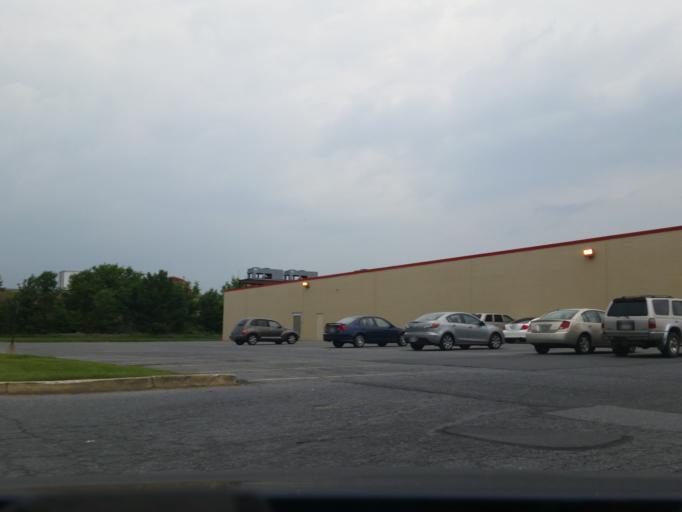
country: US
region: Pennsylvania
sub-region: Lebanon County
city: Fredericksburg
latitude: 40.4501
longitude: -76.4018
